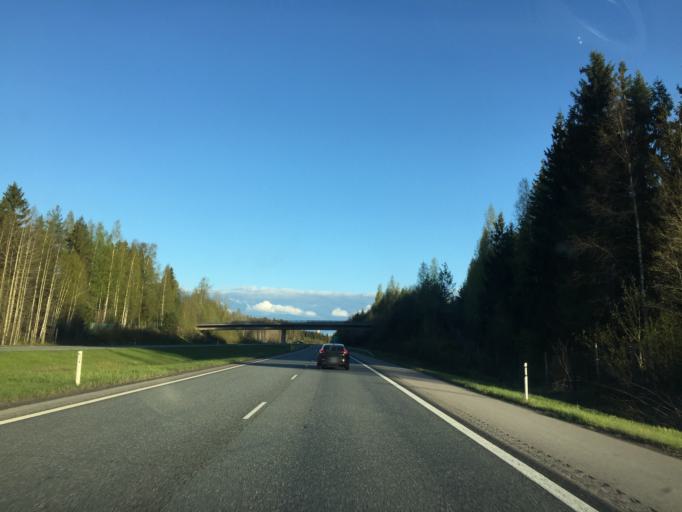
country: FI
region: Haeme
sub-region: Riihimaeki
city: Riihimaeki
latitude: 60.7670
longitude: 24.7191
